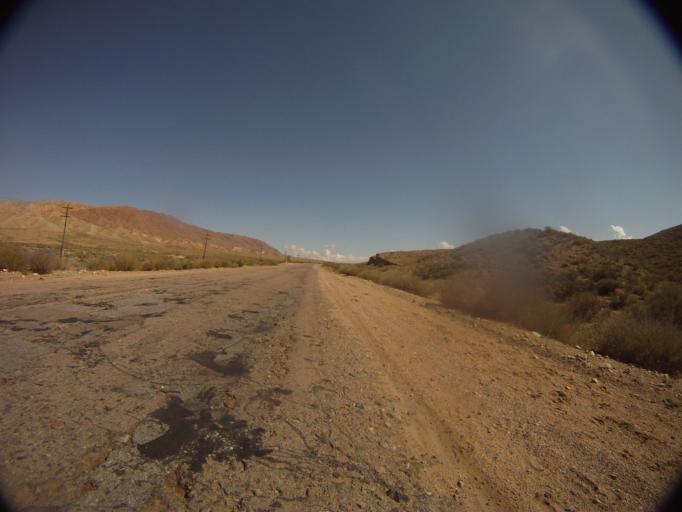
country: KG
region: Ysyk-Koel
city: Bokombayevskoye
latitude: 42.1780
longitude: 76.7005
